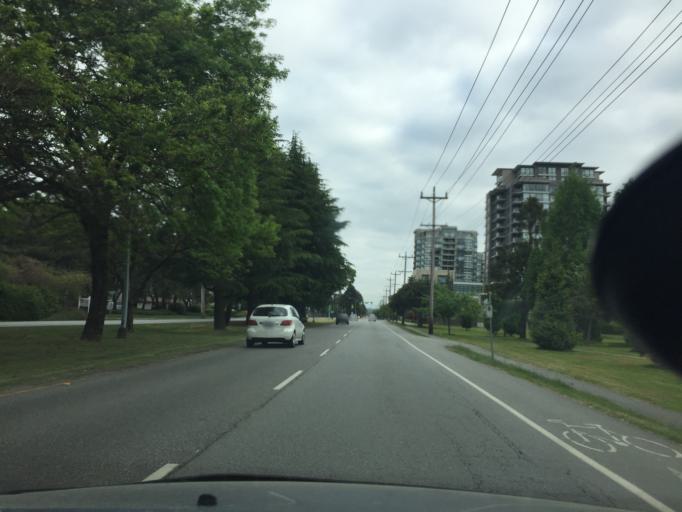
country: CA
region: British Columbia
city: Richmond
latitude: 49.1645
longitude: -123.1246
